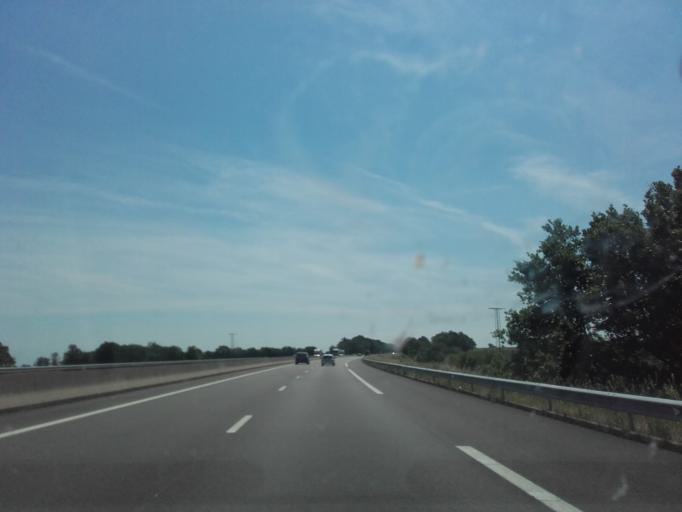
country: FR
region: Bourgogne
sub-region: Departement de la Cote-d'Or
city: Semur-en-Auxois
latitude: 47.4657
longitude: 4.2447
